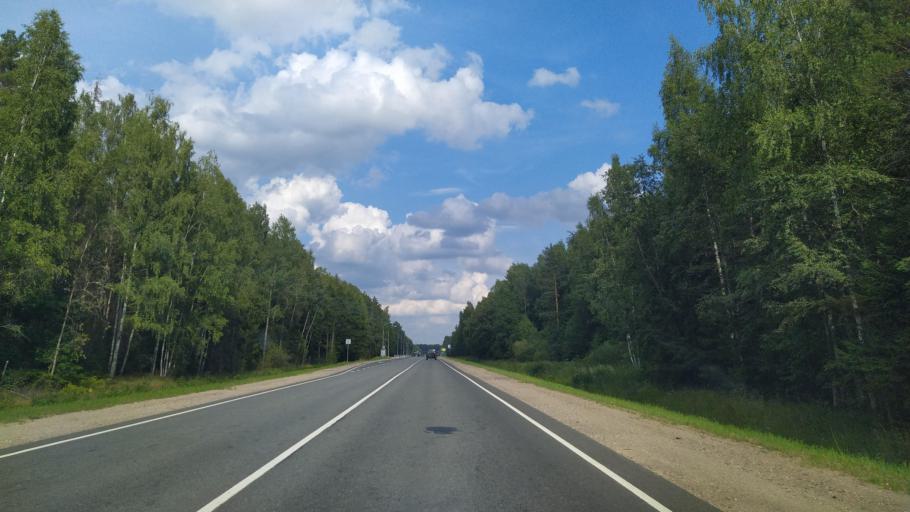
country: RU
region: Novgorod
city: Sol'tsy
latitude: 58.1723
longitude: 30.5027
